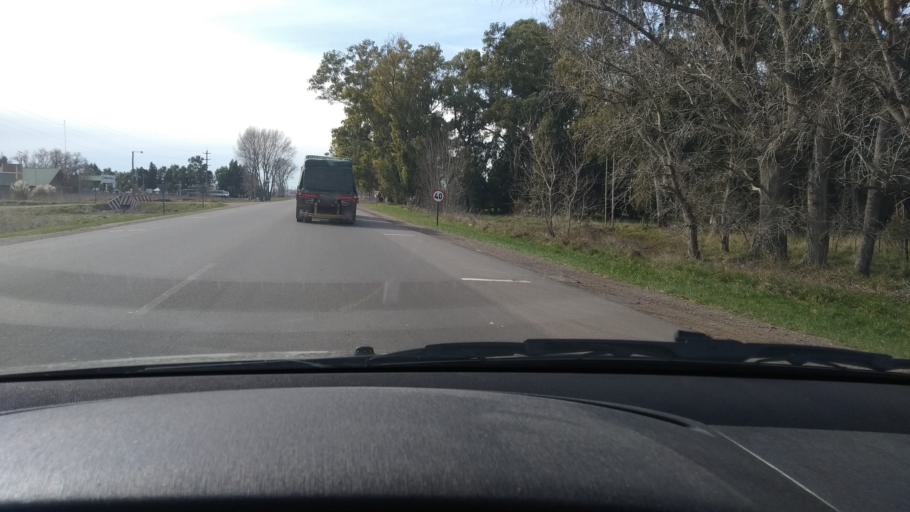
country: AR
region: Buenos Aires
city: Olavarria
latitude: -36.9477
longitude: -60.2439
